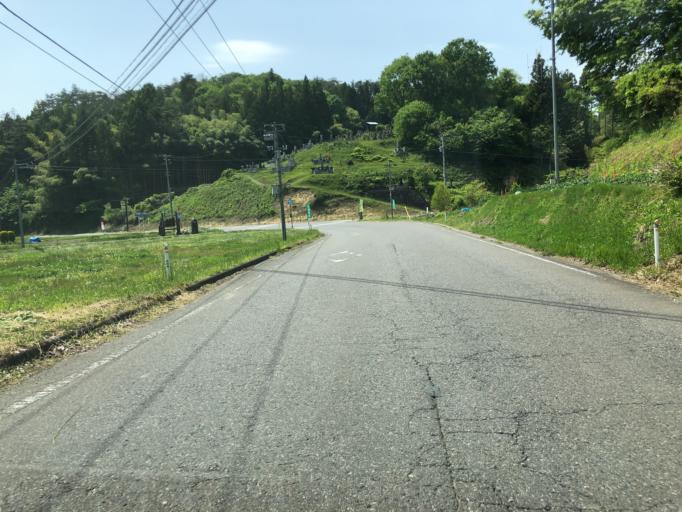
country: JP
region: Fukushima
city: Ishikawa
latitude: 37.1527
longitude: 140.5114
